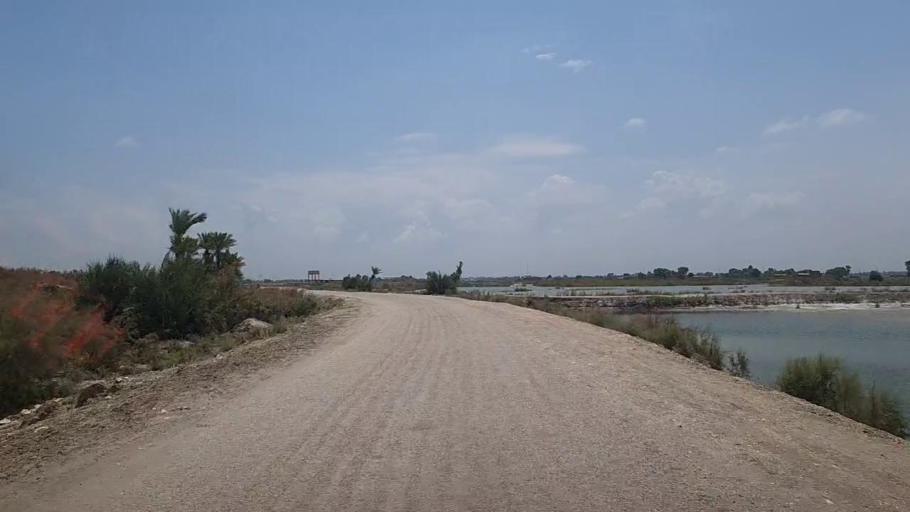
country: PK
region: Sindh
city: Kandhkot
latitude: 28.2811
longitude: 69.1706
